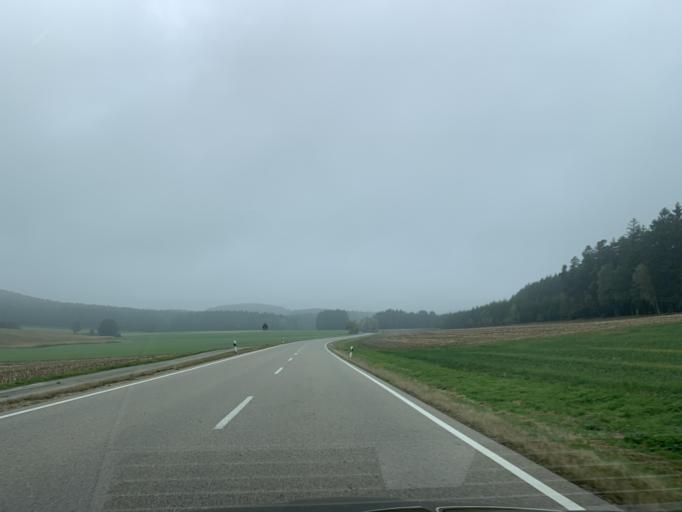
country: DE
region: Bavaria
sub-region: Upper Palatinate
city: Gleiritsch
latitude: 49.4785
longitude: 12.3398
